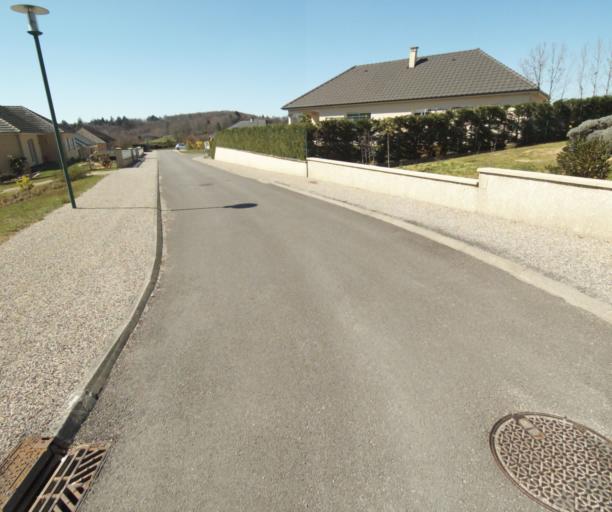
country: FR
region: Limousin
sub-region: Departement de la Correze
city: Saint-Mexant
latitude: 45.2780
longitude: 1.6553
